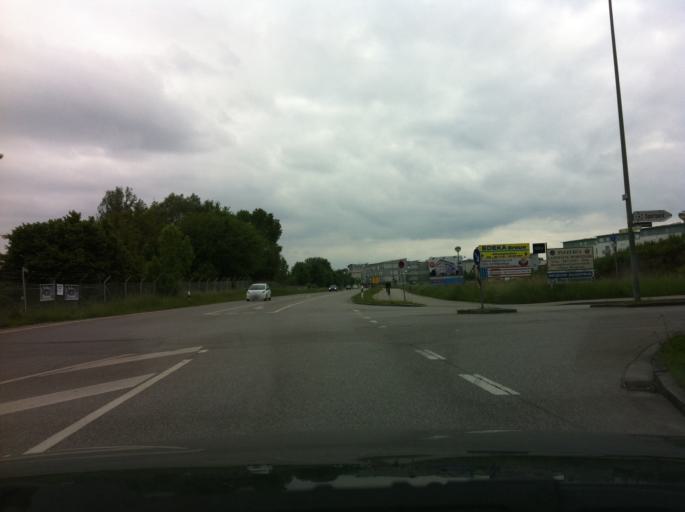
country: DE
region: Bavaria
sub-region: Upper Bavaria
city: Unterhaching
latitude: 48.0721
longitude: 11.6204
